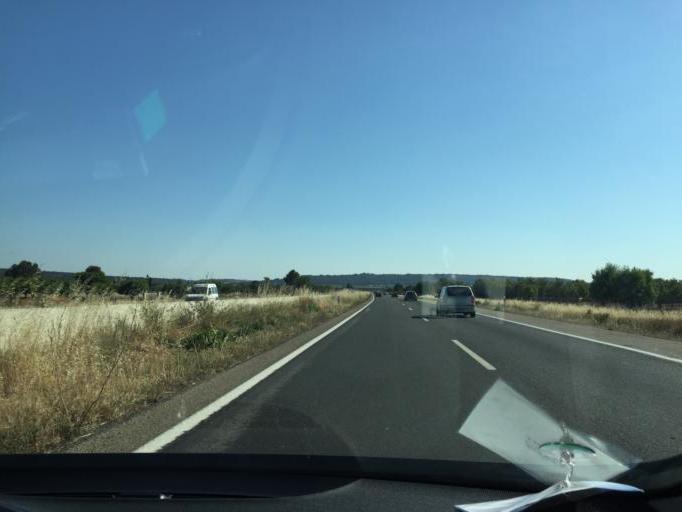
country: ES
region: Balearic Islands
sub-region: Illes Balears
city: Consell
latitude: 39.6565
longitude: 2.8033
